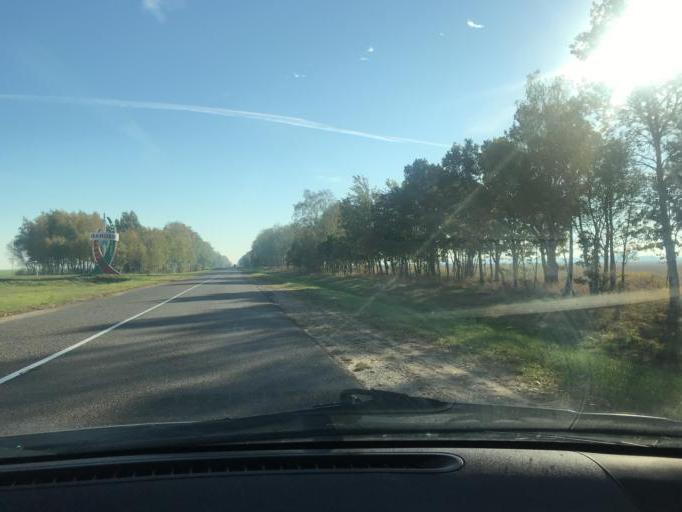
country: BY
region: Brest
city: Ivanava
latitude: 52.1459
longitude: 25.4657
